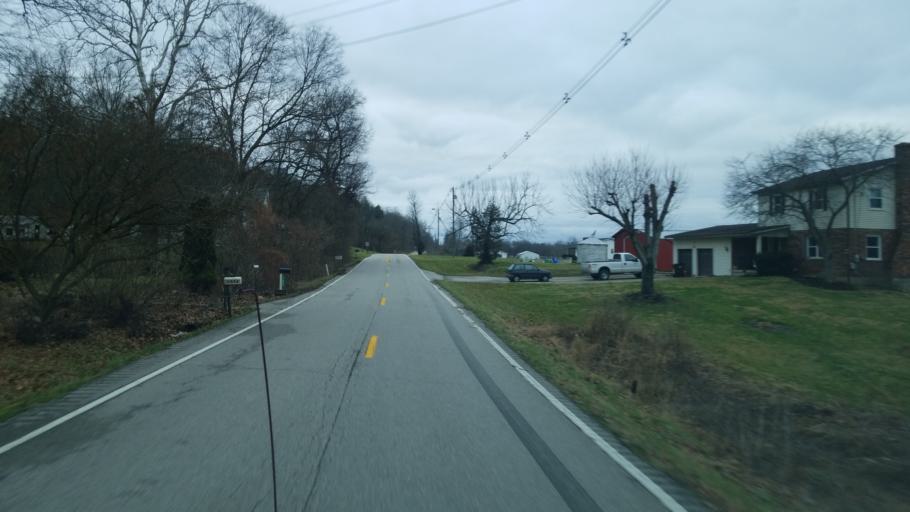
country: US
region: Ohio
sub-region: Clermont County
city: New Richmond
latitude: 38.8924
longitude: -84.2505
